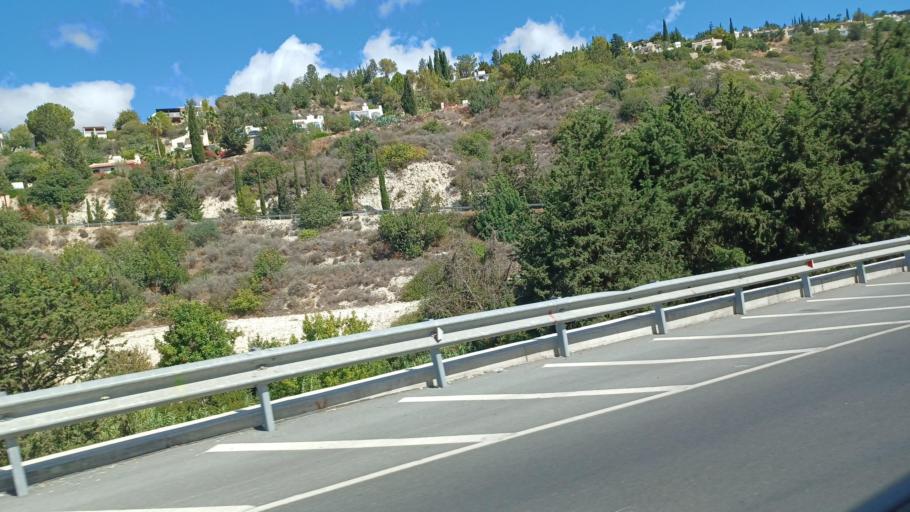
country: CY
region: Pafos
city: Tala
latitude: 34.8407
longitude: 32.4377
